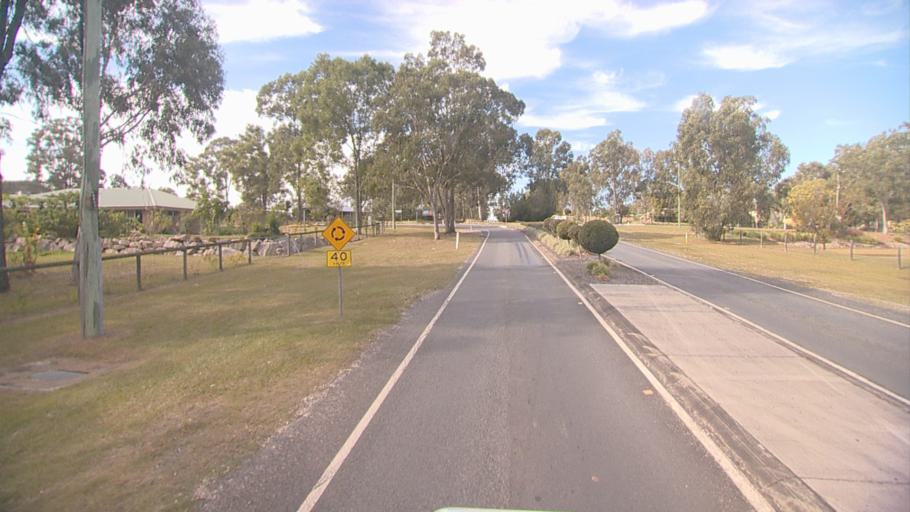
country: AU
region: Queensland
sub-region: Logan
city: North Maclean
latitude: -27.7351
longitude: 152.9593
